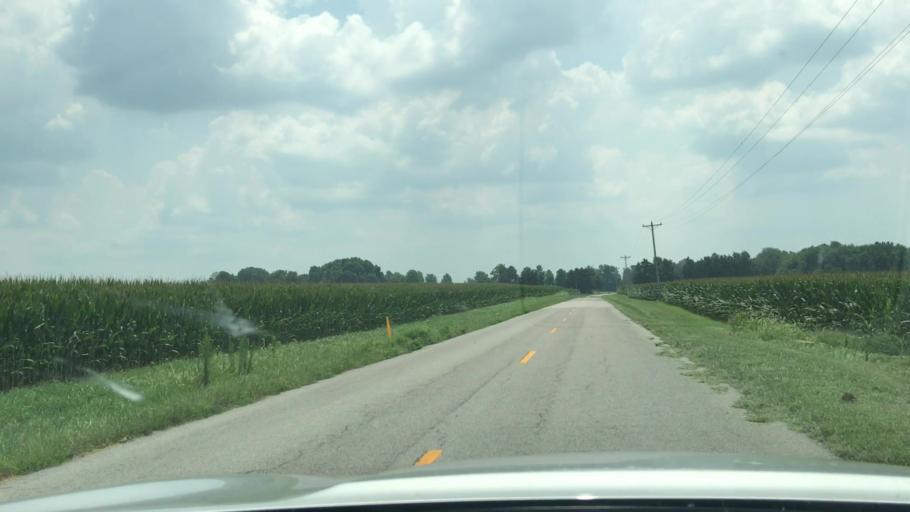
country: US
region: Kentucky
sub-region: Todd County
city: Elkton
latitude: 36.7475
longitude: -87.0956
